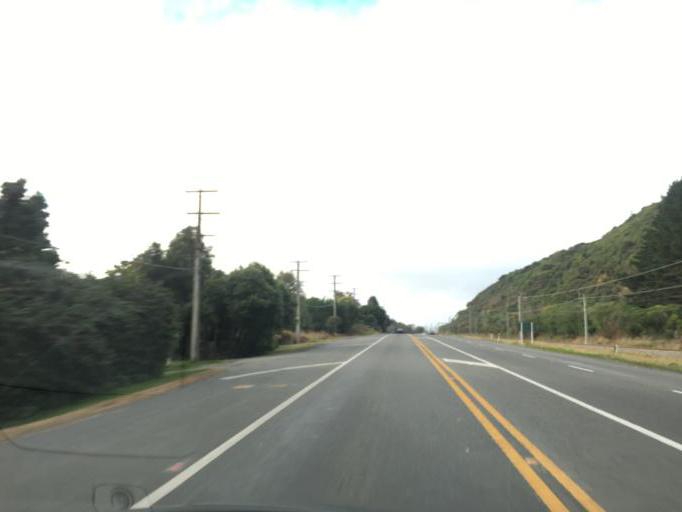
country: NZ
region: Wellington
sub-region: Kapiti Coast District
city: Paraparaumu
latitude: -40.9319
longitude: 174.9967
